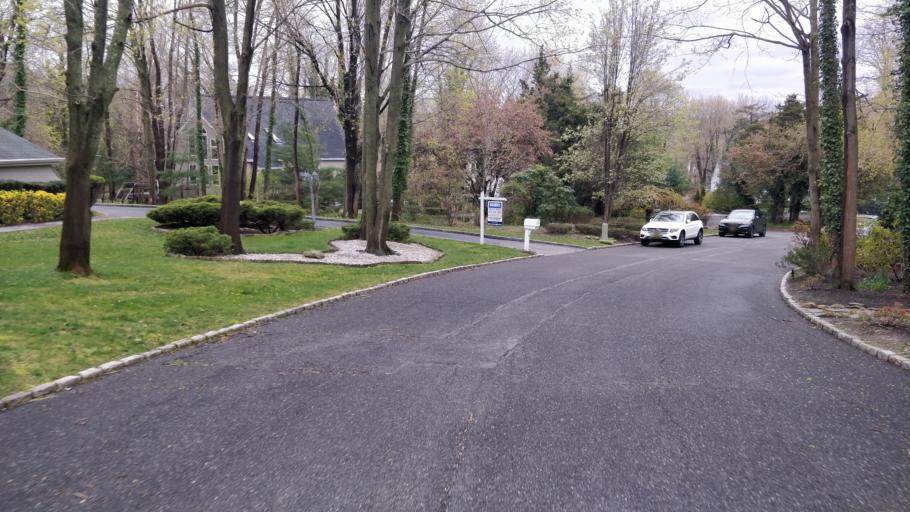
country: US
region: New York
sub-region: Suffolk County
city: East Setauket
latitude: 40.9457
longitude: -73.0962
